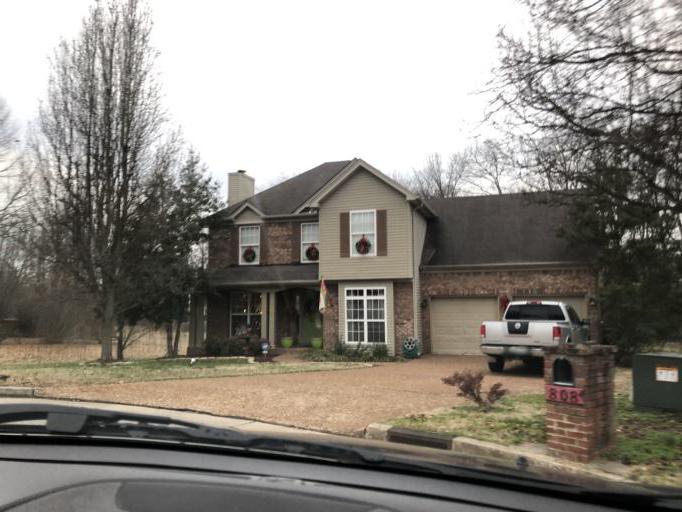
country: US
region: Tennessee
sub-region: Wilson County
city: Green Hill
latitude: 36.1997
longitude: -86.5956
